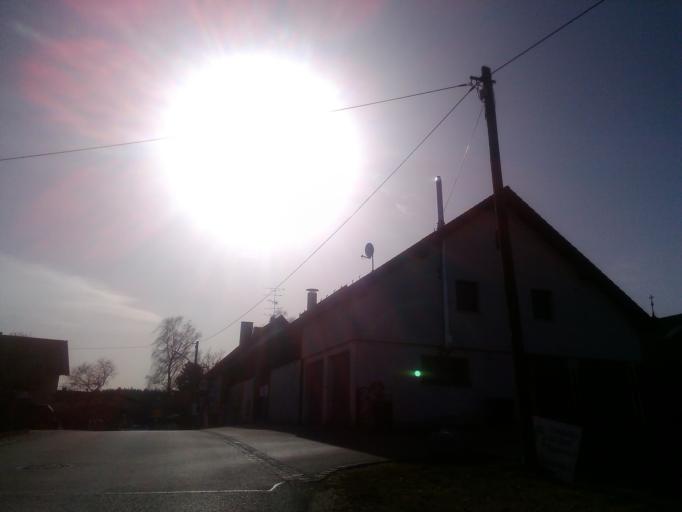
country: DE
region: Bavaria
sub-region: Upper Bavaria
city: Gilching
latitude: 48.0822
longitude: 11.3291
